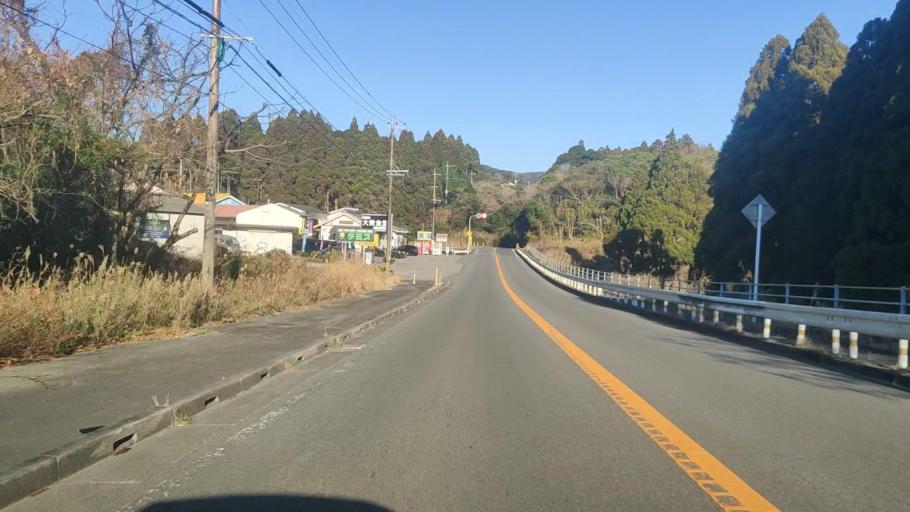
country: JP
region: Miyazaki
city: Nobeoka
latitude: 32.3456
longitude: 131.6241
